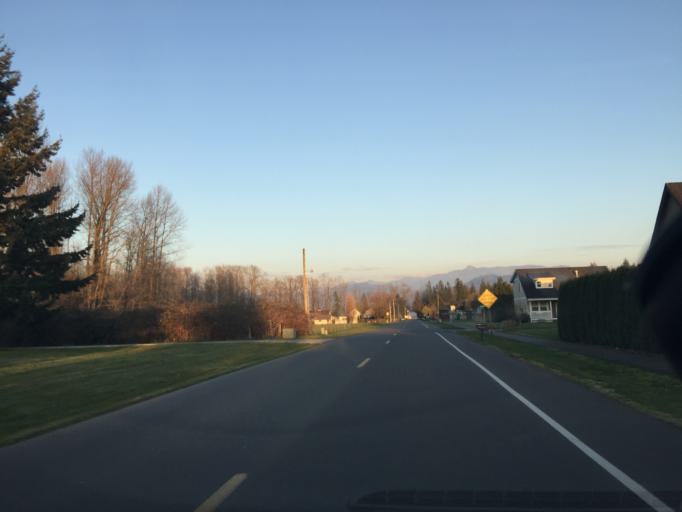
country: US
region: Washington
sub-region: Whatcom County
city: Sumas
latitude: 49.0000
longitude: -122.2574
